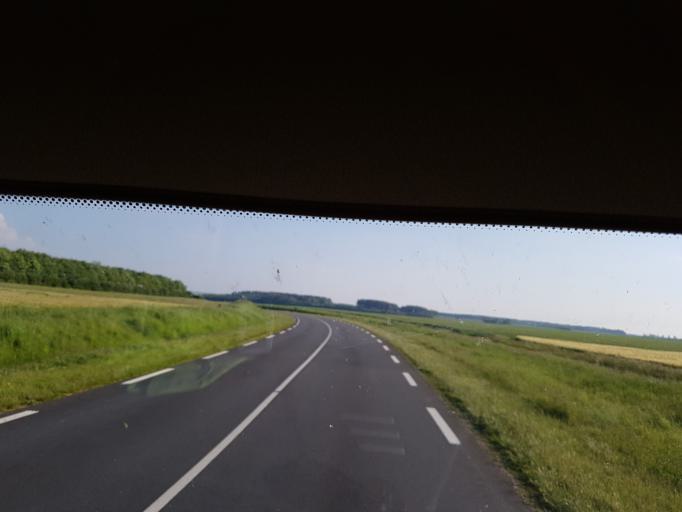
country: FR
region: Picardie
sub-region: Departement de la Somme
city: Crecy-en-Ponthieu
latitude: 50.1890
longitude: 1.8694
